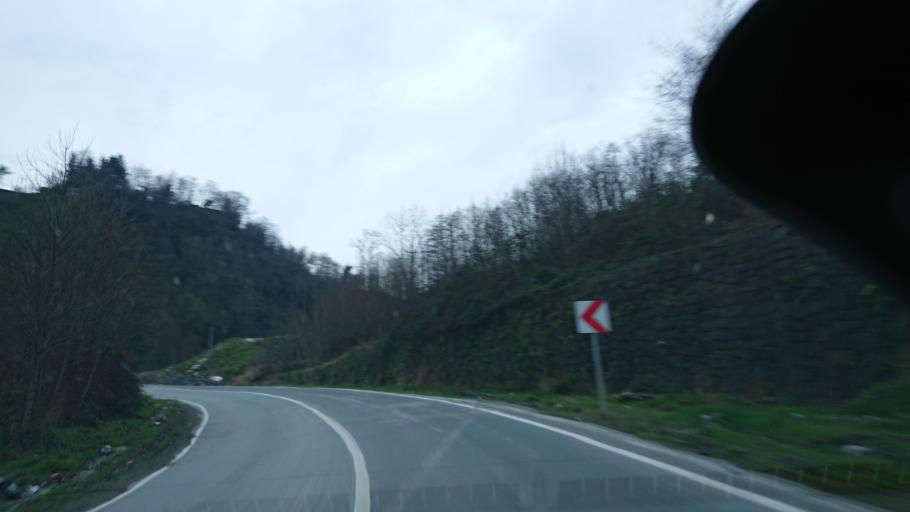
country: TR
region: Rize
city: Rize
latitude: 41.0219
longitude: 40.5022
